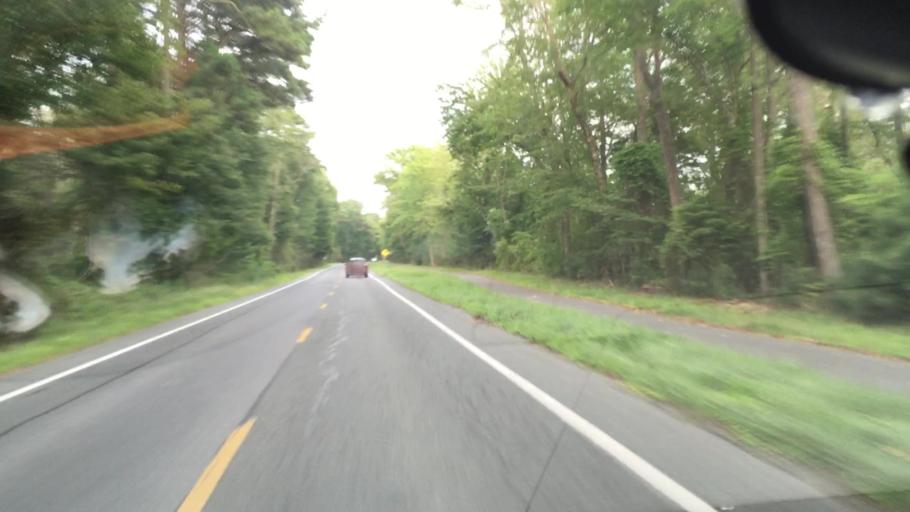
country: US
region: Delaware
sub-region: Sussex County
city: Ocean View
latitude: 38.5558
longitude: -75.0756
